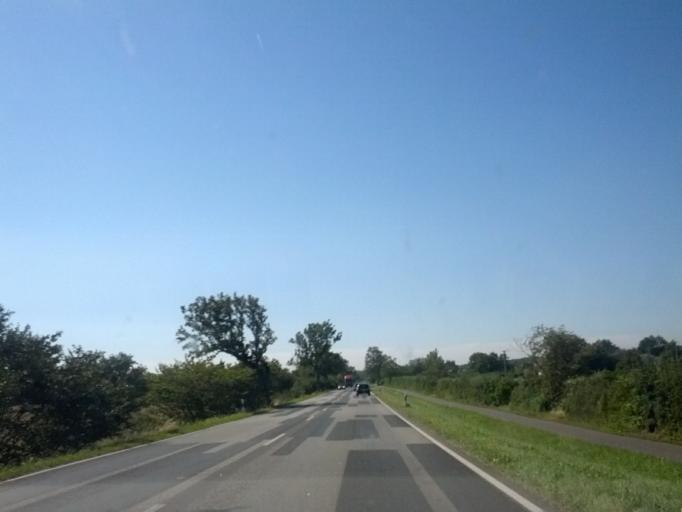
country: DE
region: Mecklenburg-Vorpommern
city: Sagard
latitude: 54.5080
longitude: 13.5338
